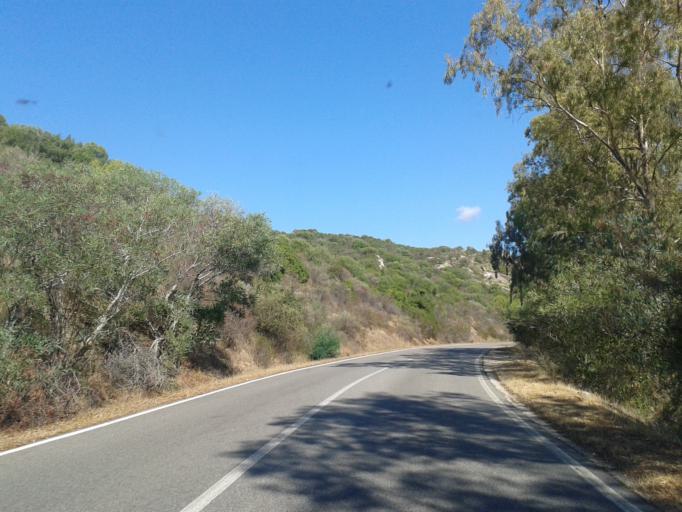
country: IT
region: Sardinia
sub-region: Provincia di Cagliari
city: Castiadas
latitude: 39.2285
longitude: 9.5586
